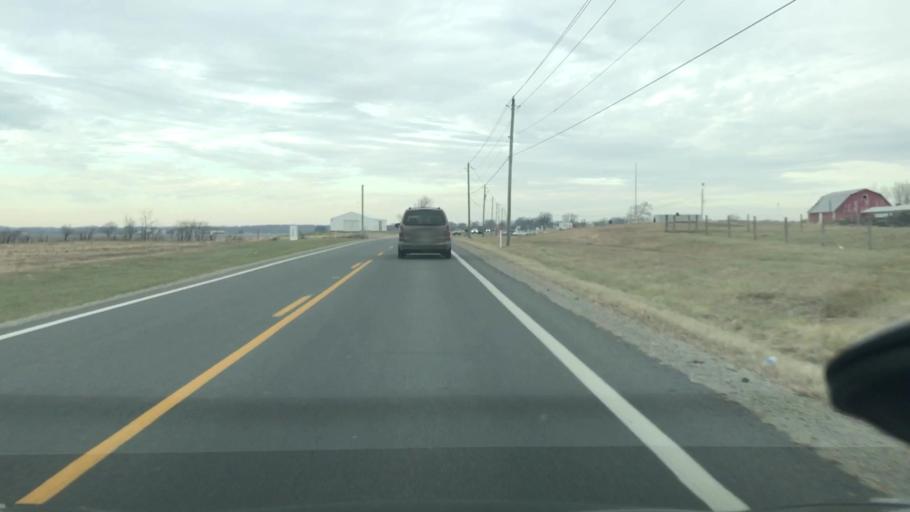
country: US
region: Ohio
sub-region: Madison County
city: Choctaw Lake
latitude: 39.9197
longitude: -83.4828
